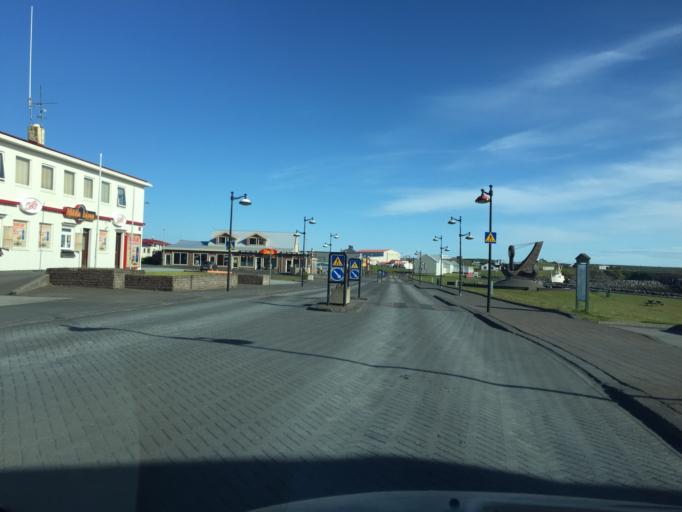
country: IS
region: Southern Peninsula
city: Reykjanesbaer
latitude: 64.0047
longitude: -22.5560
